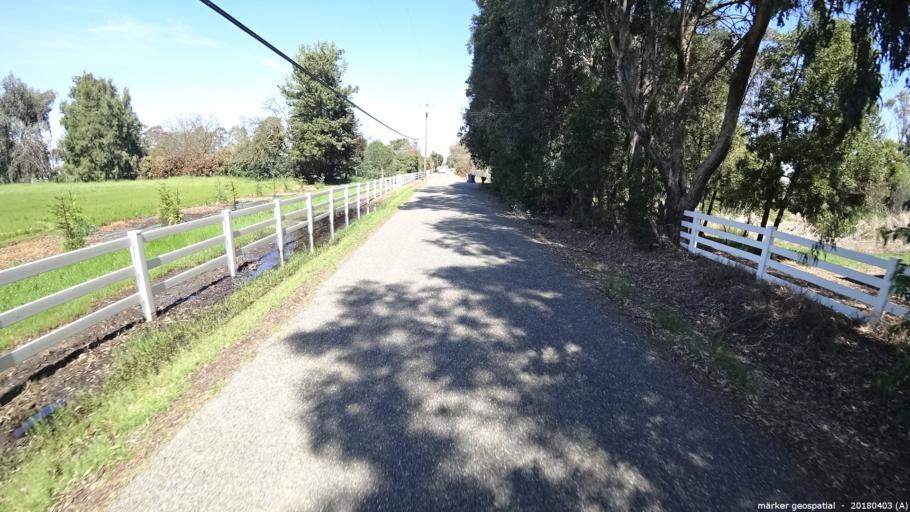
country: US
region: California
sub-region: Sacramento County
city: Wilton
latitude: 38.3885
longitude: -121.2699
